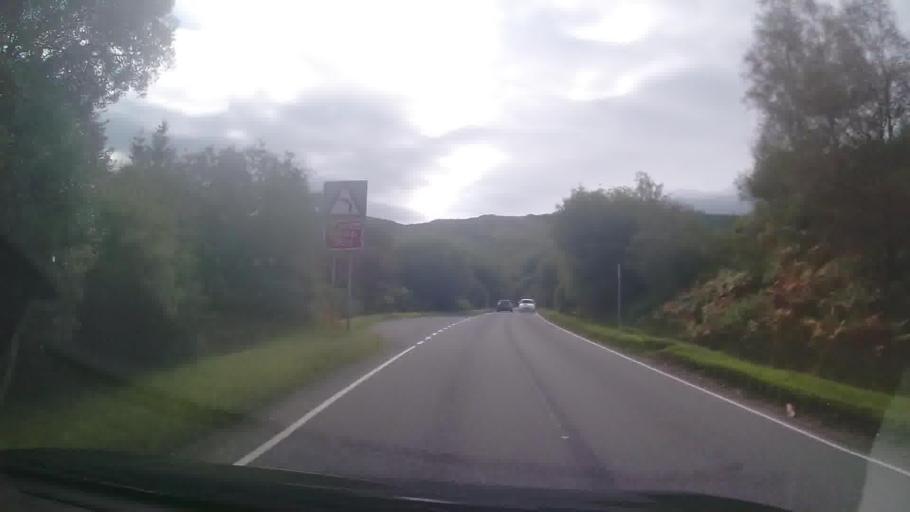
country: GB
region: Scotland
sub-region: Argyll and Bute
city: Garelochhead
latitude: 56.3204
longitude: -5.0818
